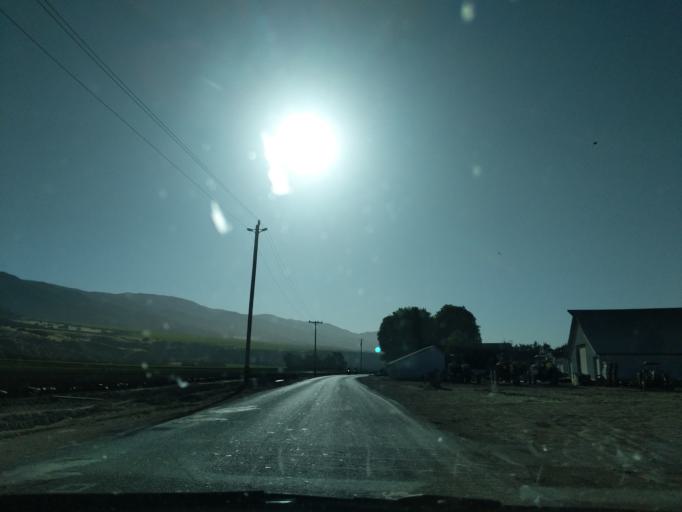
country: US
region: California
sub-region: Monterey County
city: Soledad
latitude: 36.4087
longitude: -121.3744
